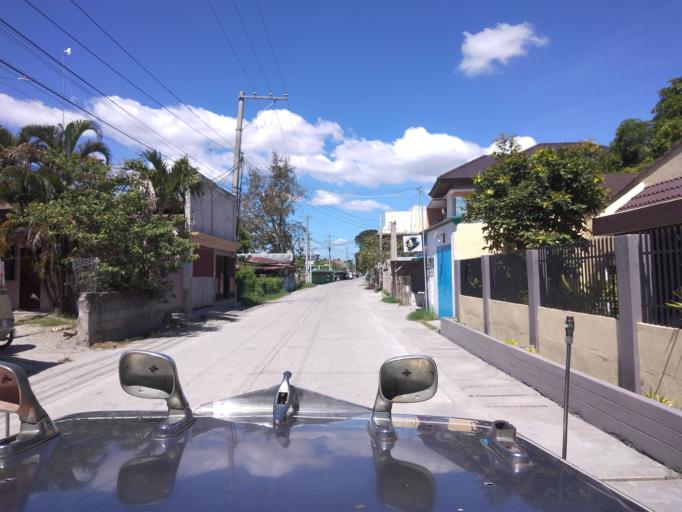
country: PH
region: Central Luzon
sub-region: Province of Pampanga
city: Magliman
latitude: 15.0363
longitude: 120.6465
